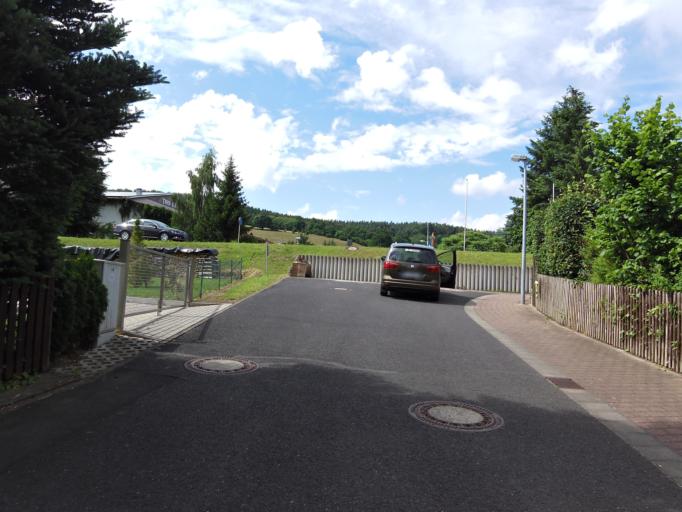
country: DE
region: Thuringia
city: Dorndorf
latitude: 50.8429
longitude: 10.1178
